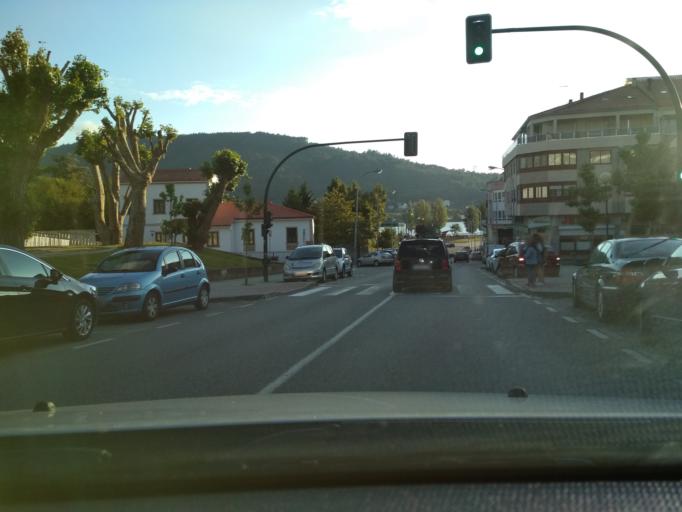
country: ES
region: Galicia
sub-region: Provincia da Coruna
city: Noia
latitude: 42.7863
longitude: -8.8888
